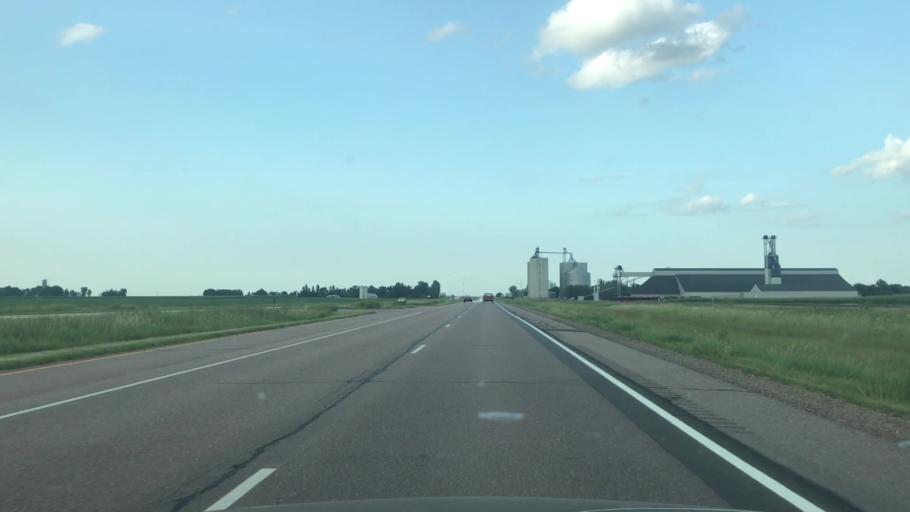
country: US
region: Minnesota
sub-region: Nobles County
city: Worthington
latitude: 43.6915
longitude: -95.4824
